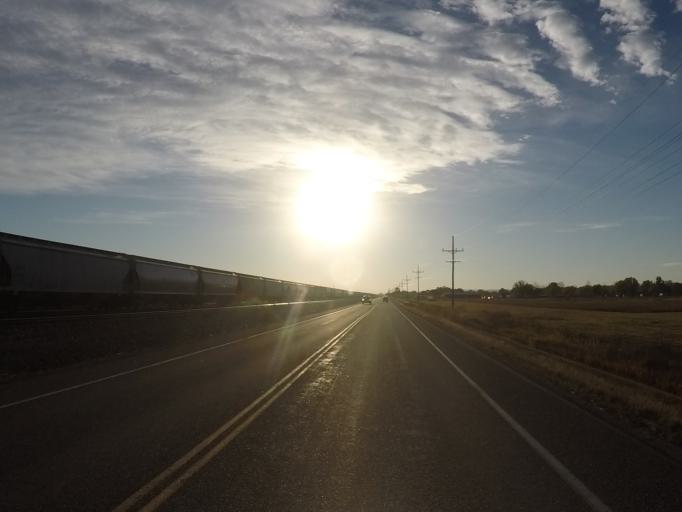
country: US
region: Montana
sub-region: Yellowstone County
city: Laurel
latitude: 45.6808
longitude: -108.7235
